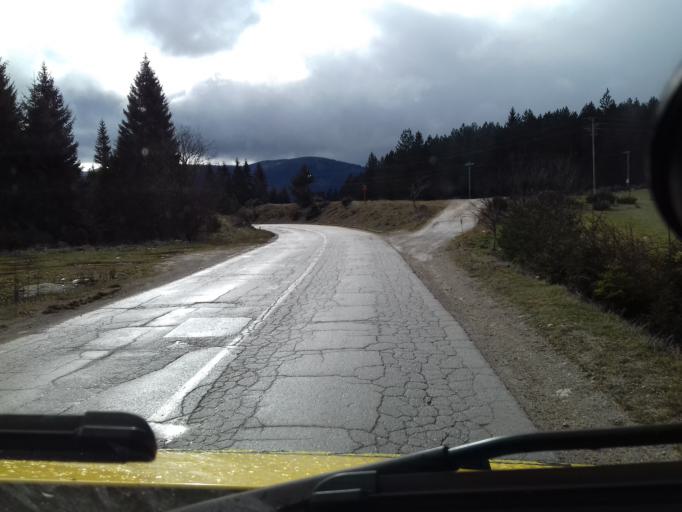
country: BA
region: Federation of Bosnia and Herzegovina
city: Turbe
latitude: 44.2874
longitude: 17.5003
